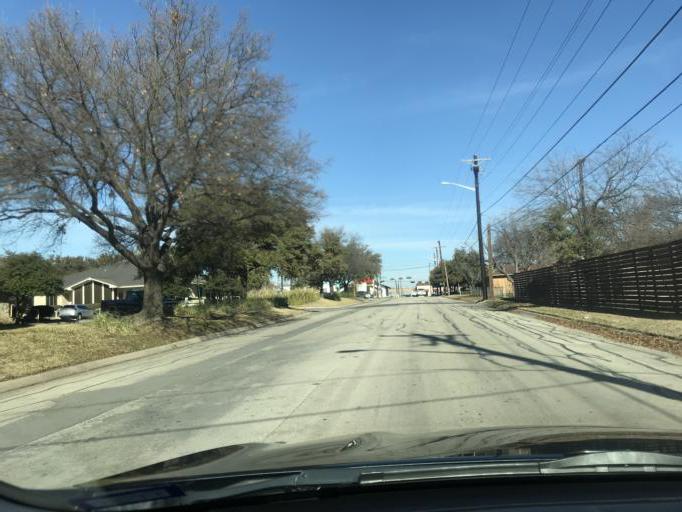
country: US
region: Texas
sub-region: Denton County
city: Denton
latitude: 33.2277
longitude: -97.1432
